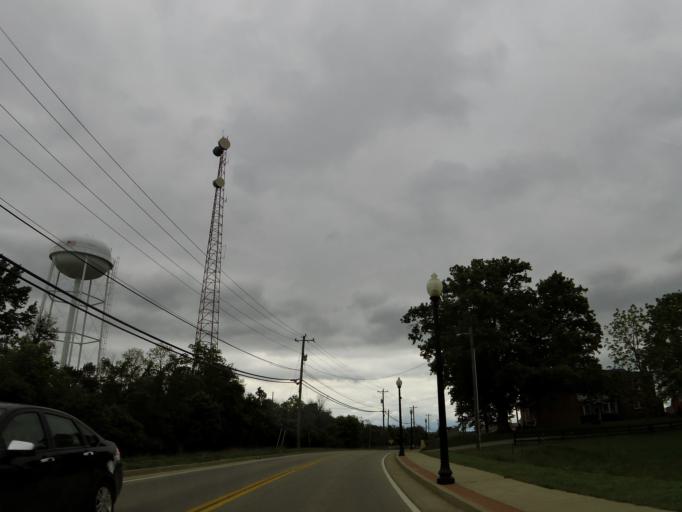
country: US
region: Kentucky
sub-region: Grant County
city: Williamstown
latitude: 38.6331
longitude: -84.5658
